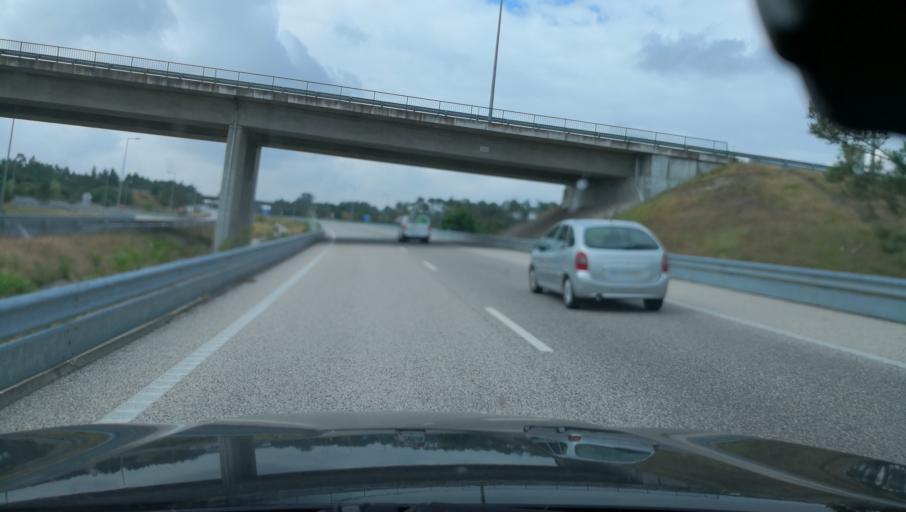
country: PT
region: Coimbra
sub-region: Montemor-O-Velho
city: Arazede
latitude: 40.3272
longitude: -8.7224
